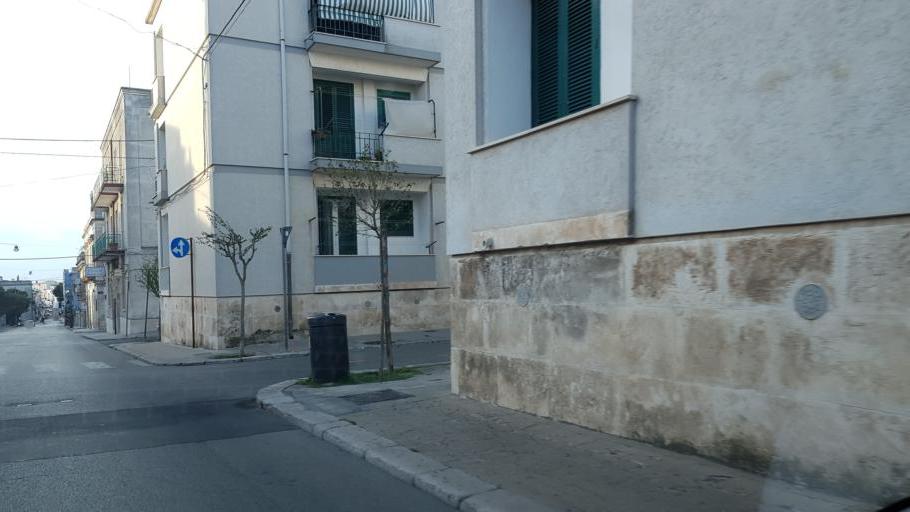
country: IT
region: Apulia
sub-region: Provincia di Taranto
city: Martina Franca
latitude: 40.7019
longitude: 17.3429
